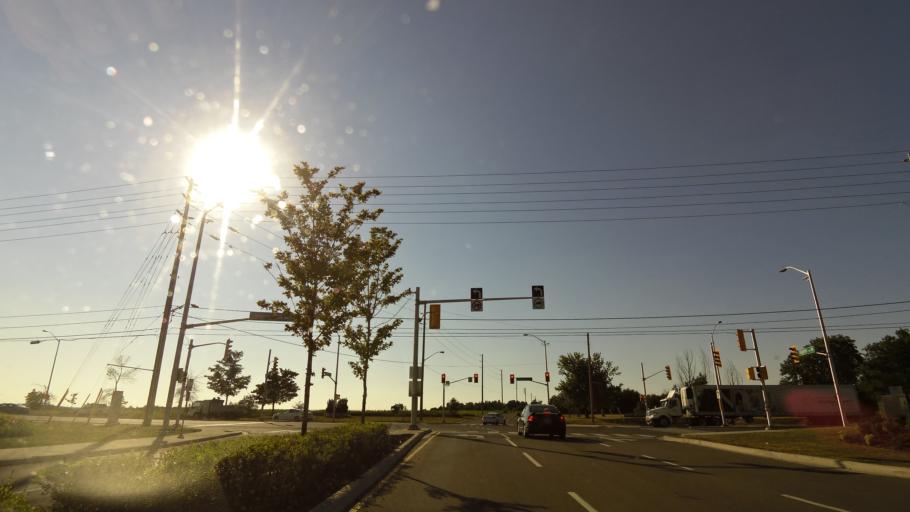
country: CA
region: Ontario
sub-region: Halton
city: Milton
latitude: 43.5779
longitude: -79.8300
